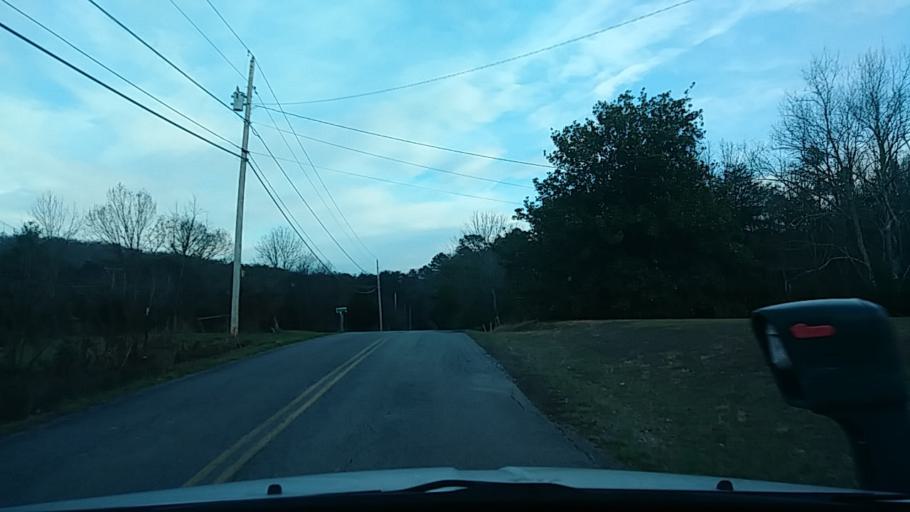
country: US
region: Tennessee
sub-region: Greene County
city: Mosheim
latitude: 36.1159
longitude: -82.9342
